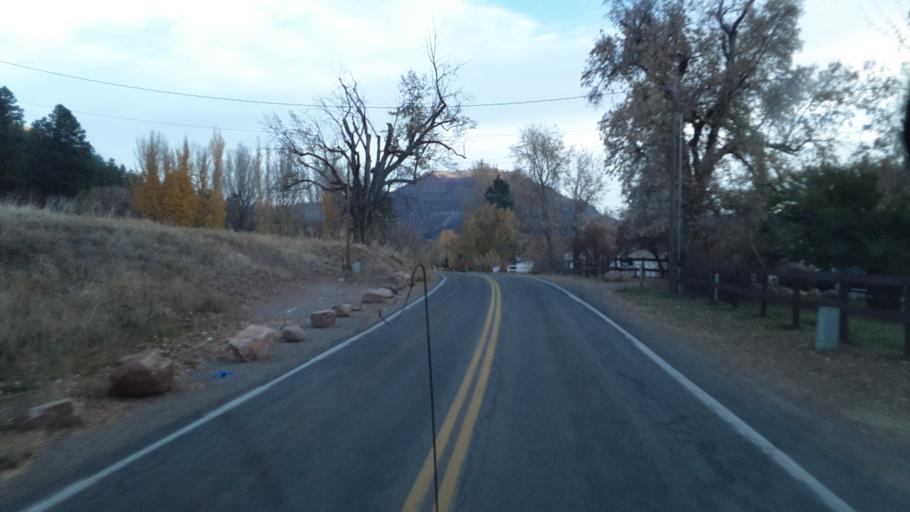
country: US
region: Colorado
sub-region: La Plata County
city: Durango
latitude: 37.3925
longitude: -107.8477
